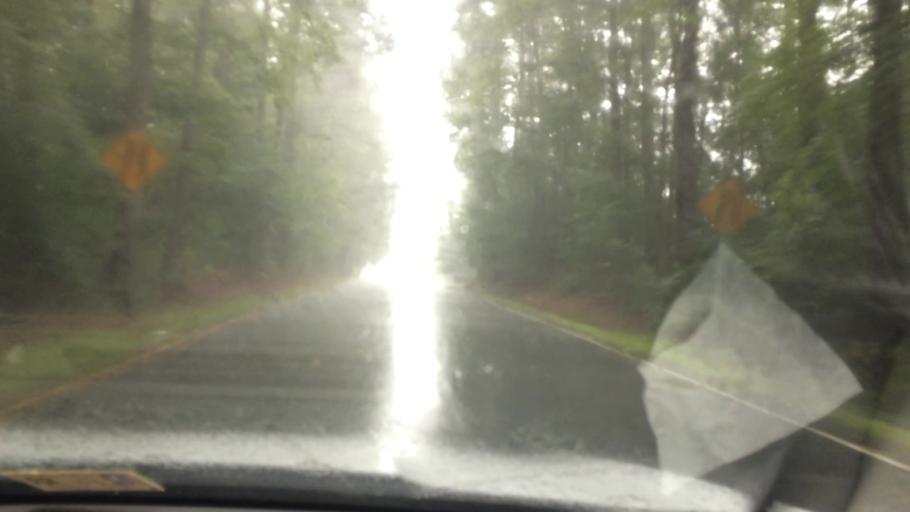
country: US
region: Virginia
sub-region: James City County
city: Williamsburg
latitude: 37.3928
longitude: -76.7745
